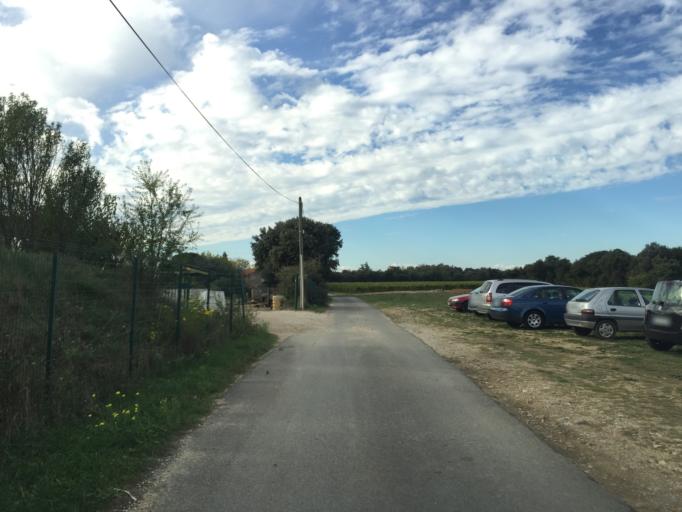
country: FR
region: Provence-Alpes-Cote d'Azur
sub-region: Departement du Vaucluse
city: Orange
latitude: 44.1108
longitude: 4.8203
